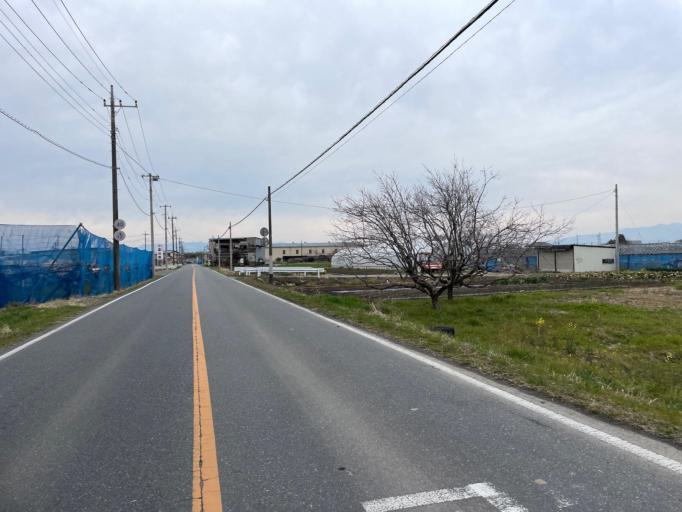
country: JP
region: Gunma
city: Fujioka
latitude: 36.2270
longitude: 139.1006
